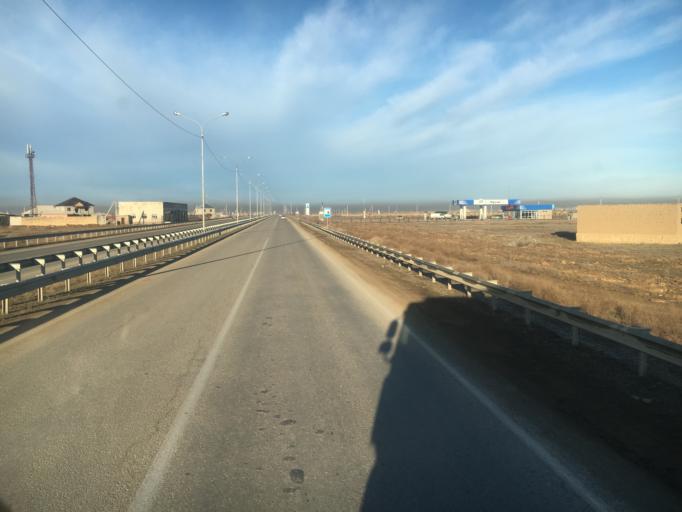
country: KZ
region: Ongtustik Qazaqstan
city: Turkestan
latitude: 43.3016
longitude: 68.3343
